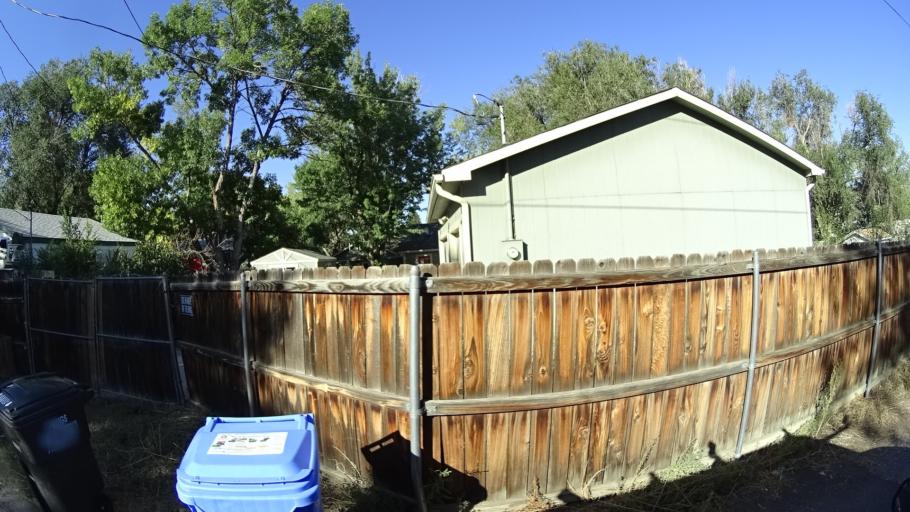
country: US
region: Colorado
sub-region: El Paso County
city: Colorado Springs
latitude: 38.8408
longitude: -104.8694
